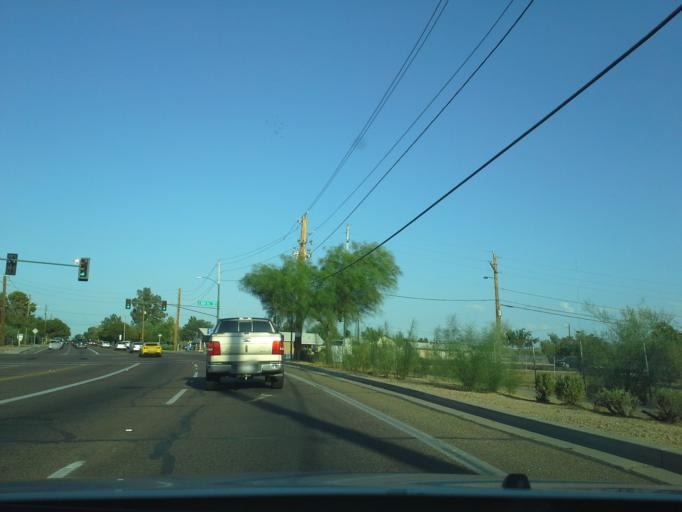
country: US
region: Arizona
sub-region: Maricopa County
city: Guadalupe
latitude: 33.3926
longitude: -112.0133
